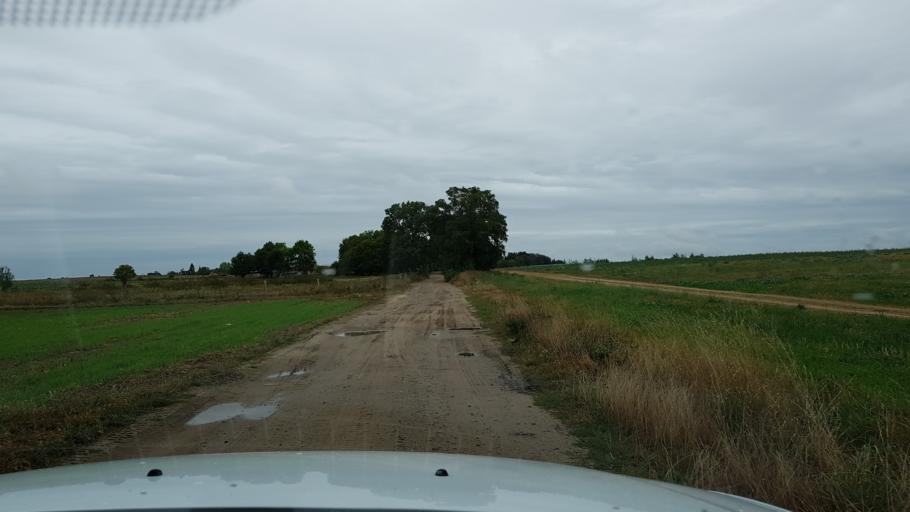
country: PL
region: West Pomeranian Voivodeship
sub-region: Powiat gryfinski
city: Moryn
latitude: 52.8422
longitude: 14.3000
